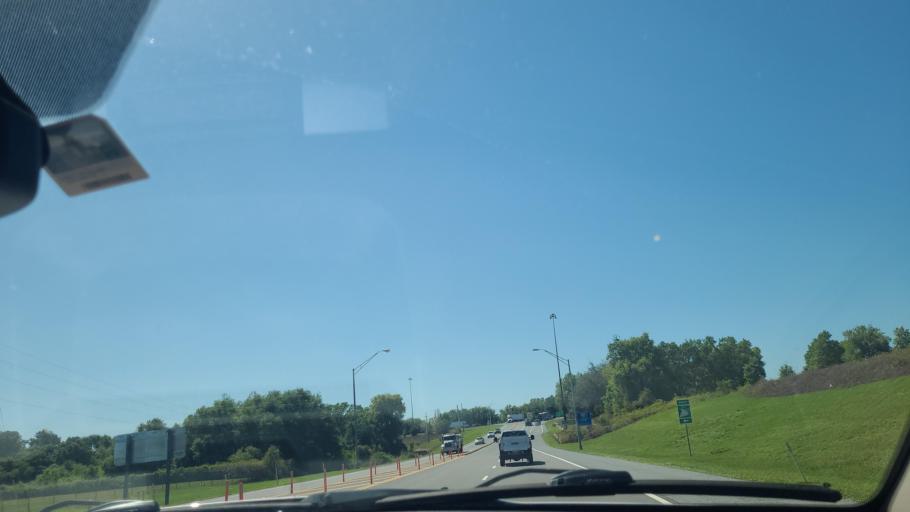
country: US
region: Florida
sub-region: Lake County
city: Howie In The Hills
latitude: 28.6465
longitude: -81.8093
